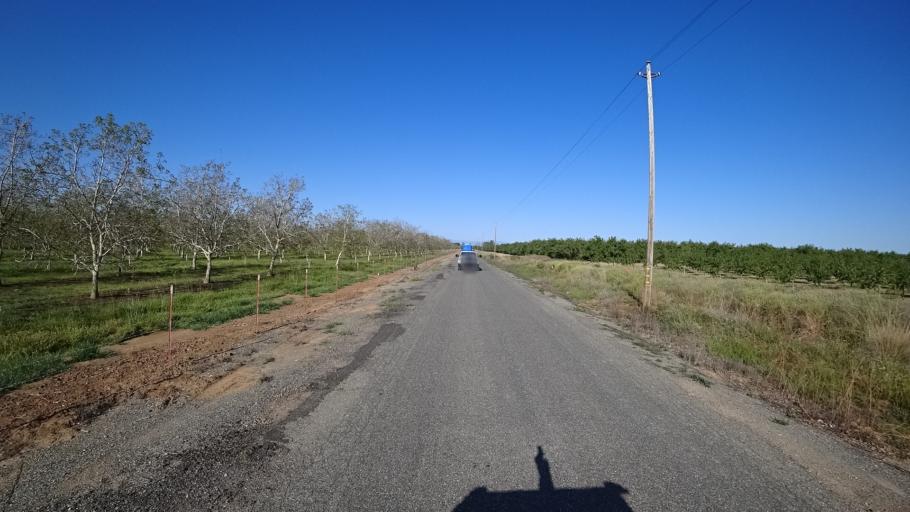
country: US
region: California
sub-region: Glenn County
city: Hamilton City
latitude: 39.6960
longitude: -122.0753
